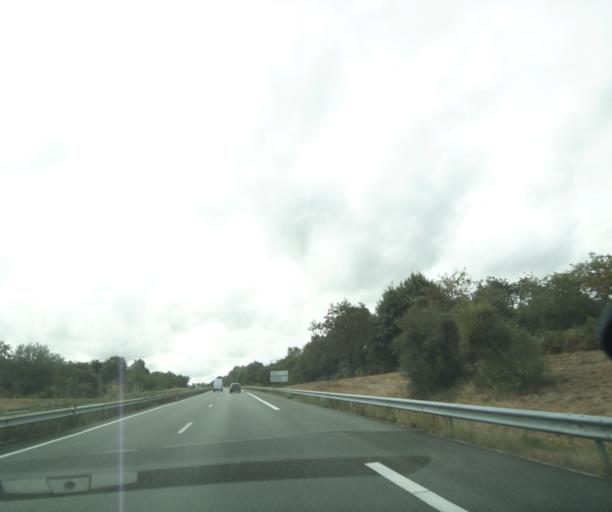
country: FR
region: Poitou-Charentes
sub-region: Departement de la Charente-Maritime
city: Saint-Genis-de-Saintonge
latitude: 45.4654
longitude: -0.6202
